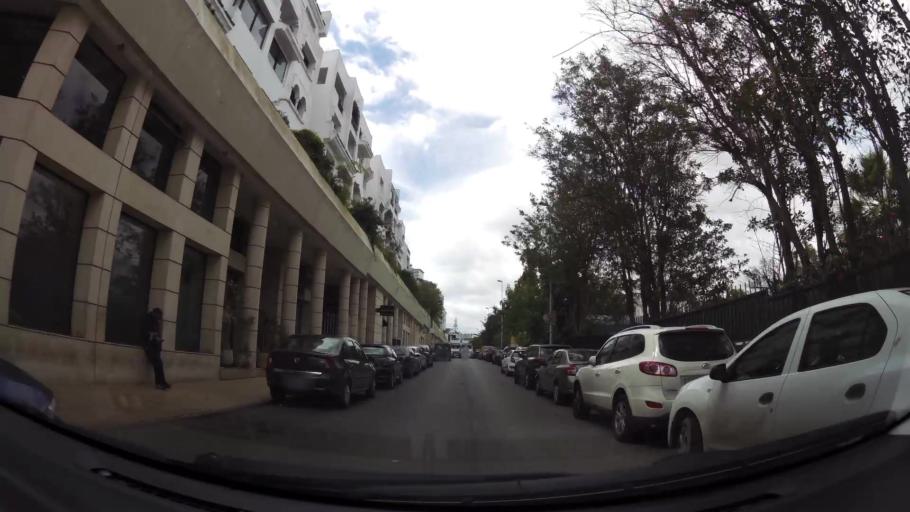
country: MA
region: Grand Casablanca
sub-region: Casablanca
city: Casablanca
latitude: 33.5773
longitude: -7.6513
